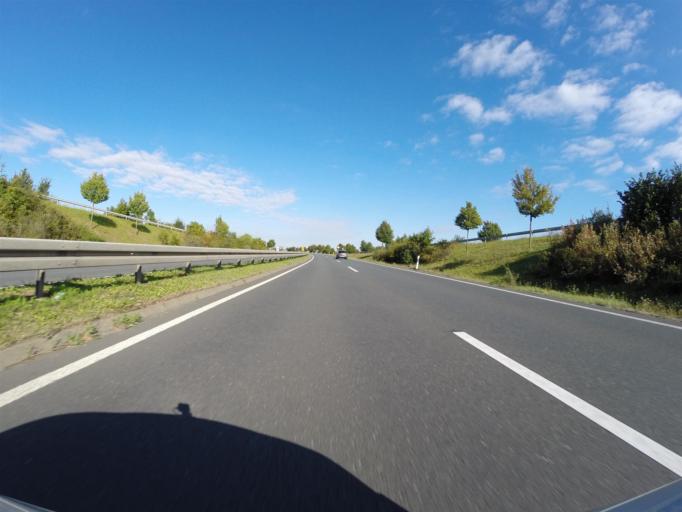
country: DE
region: Thuringia
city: Monchenholzhausen
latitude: 50.9706
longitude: 11.1364
